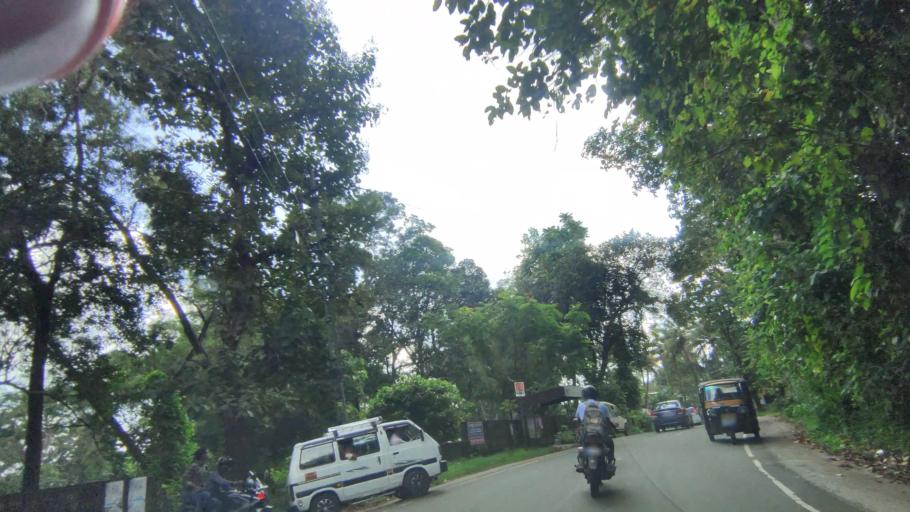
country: IN
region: Kerala
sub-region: Kottayam
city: Kottayam
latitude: 9.6765
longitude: 76.5422
